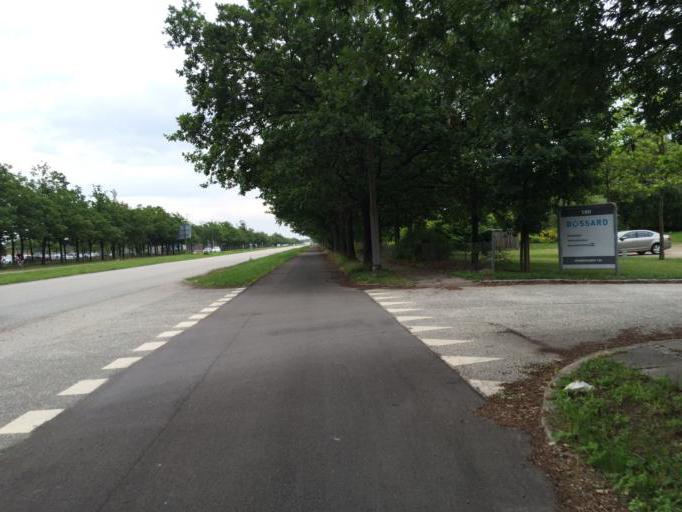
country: DK
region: Capital Region
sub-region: Hvidovre Kommune
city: Hvidovre
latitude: 55.6139
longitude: 12.4770
